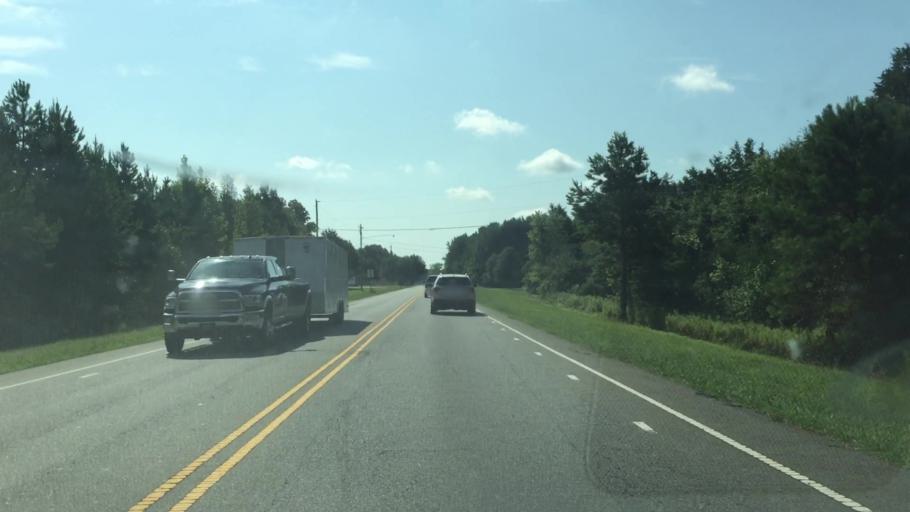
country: US
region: North Carolina
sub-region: Mecklenburg County
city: Mint Hill
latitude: 35.1756
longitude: -80.6232
